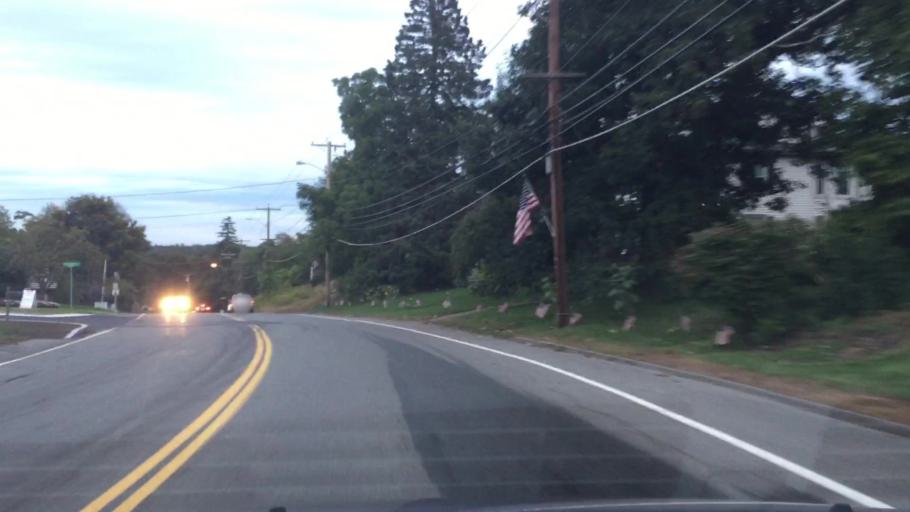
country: US
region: Massachusetts
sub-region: Essex County
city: Haverhill
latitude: 42.7999
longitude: -71.0831
